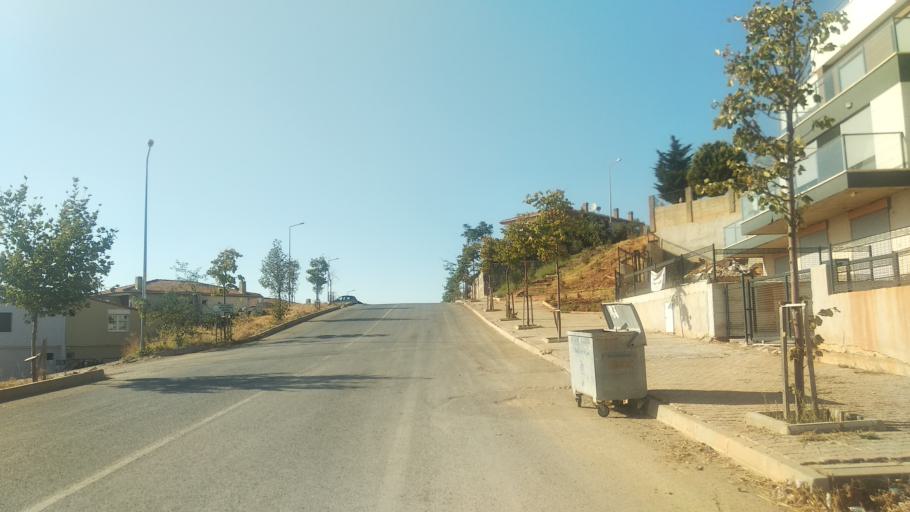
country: TR
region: Izmir
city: Urla
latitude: 38.3588
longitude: 26.8804
